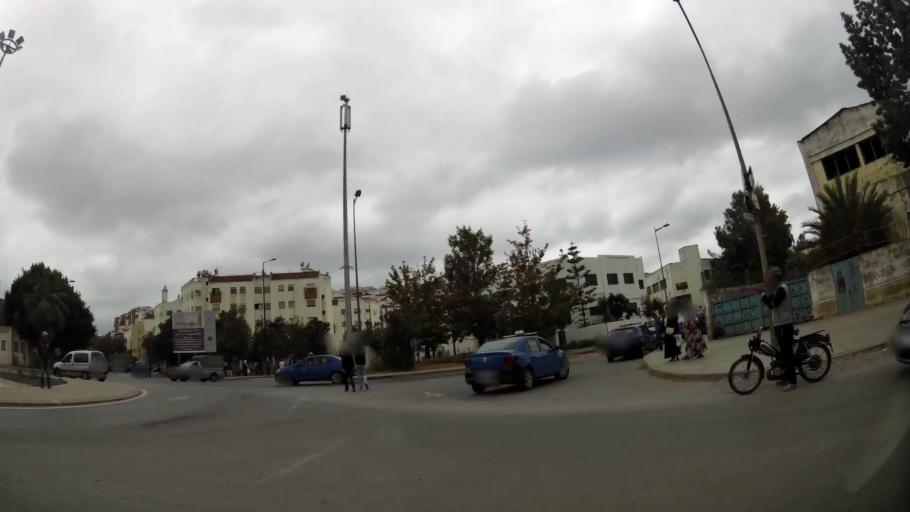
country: MA
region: Rabat-Sale-Zemmour-Zaer
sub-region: Rabat
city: Rabat
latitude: 33.9872
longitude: -6.8037
